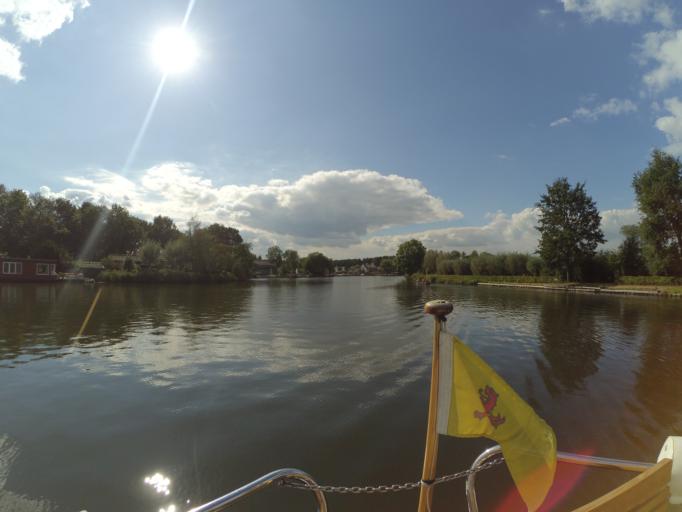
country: NL
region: Utrecht
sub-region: Stichtse Vecht
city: Breukelen
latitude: 52.1974
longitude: 5.0154
